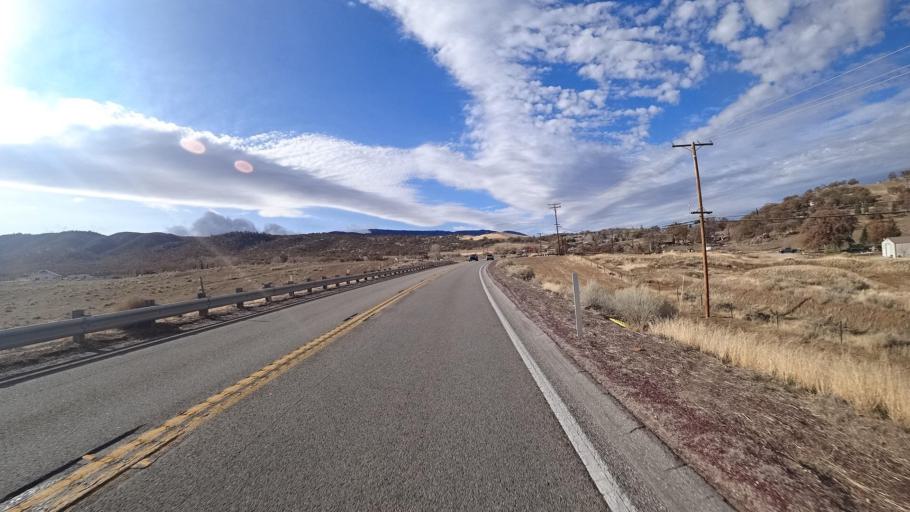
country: US
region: California
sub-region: Kern County
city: Golden Hills
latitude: 35.1128
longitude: -118.5102
